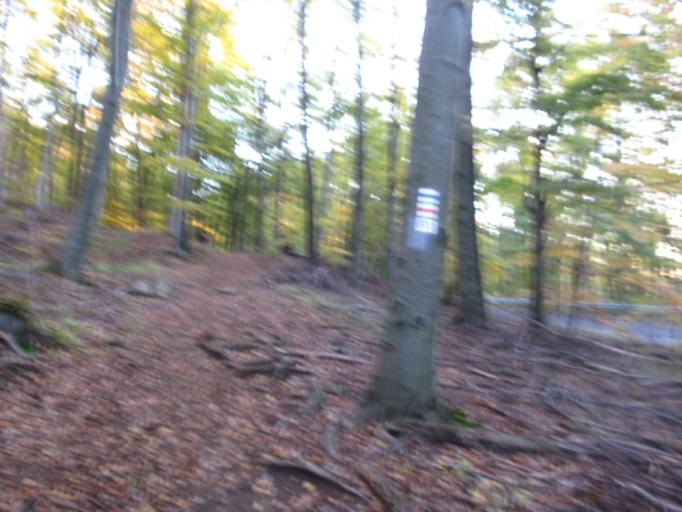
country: HU
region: Heves
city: Paradsasvar
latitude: 47.8878
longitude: 19.9749
